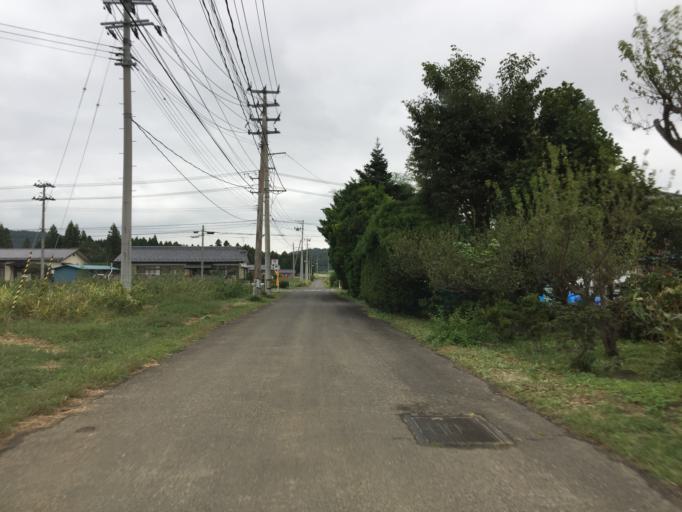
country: JP
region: Fukushima
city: Nihommatsu
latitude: 37.6524
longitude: 140.4521
